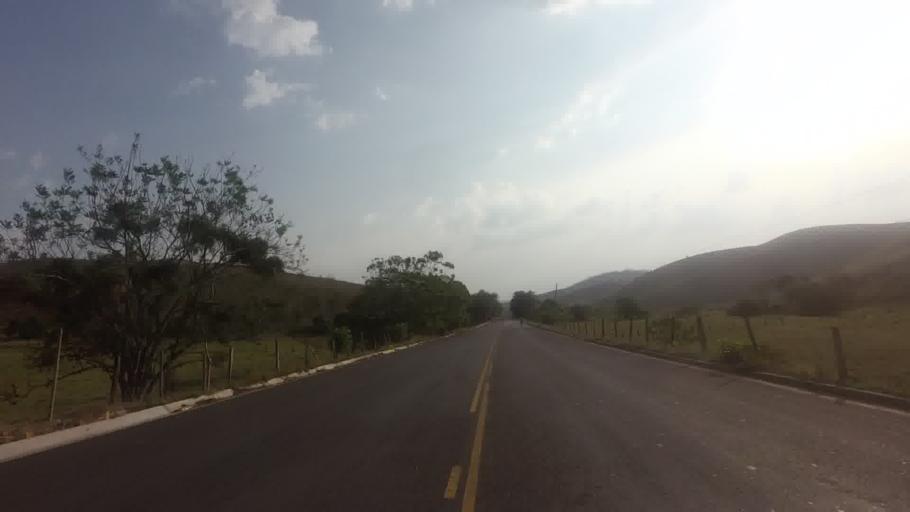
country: BR
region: Rio de Janeiro
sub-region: Itaperuna
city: Itaperuna
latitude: -21.3734
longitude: -41.9485
